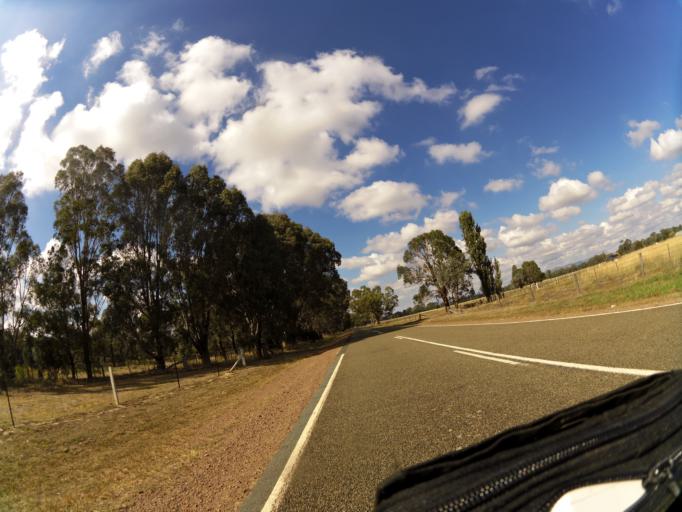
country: AU
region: Victoria
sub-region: Benalla
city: Benalla
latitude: -36.5851
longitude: 146.0082
